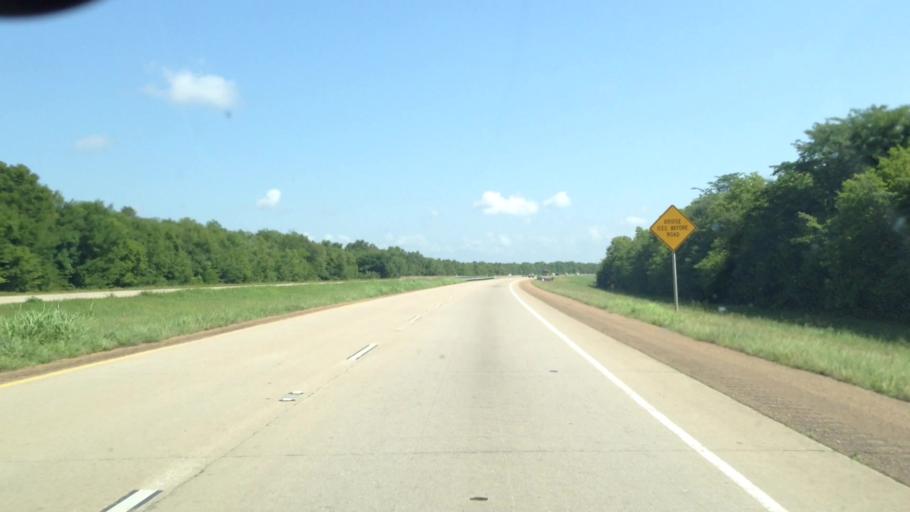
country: US
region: Louisiana
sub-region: Rapides Parish
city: Woodworth
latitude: 31.1952
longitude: -92.4740
